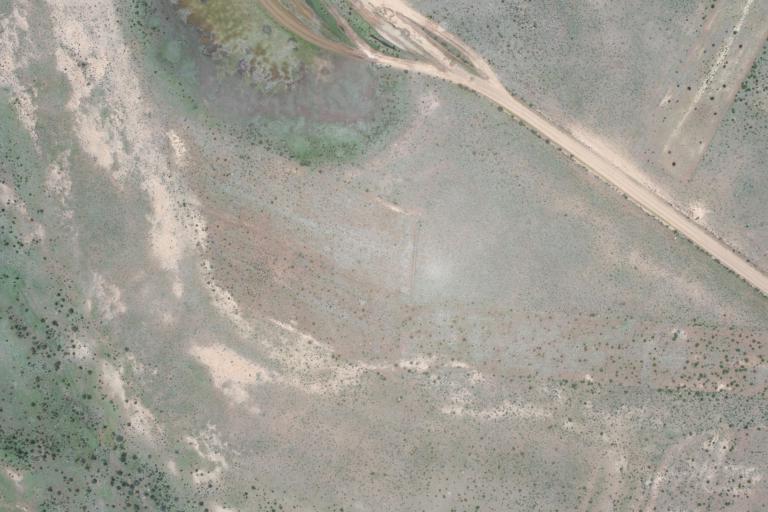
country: BO
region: La Paz
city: Curahuara de Carangas
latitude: -17.2826
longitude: -68.5121
